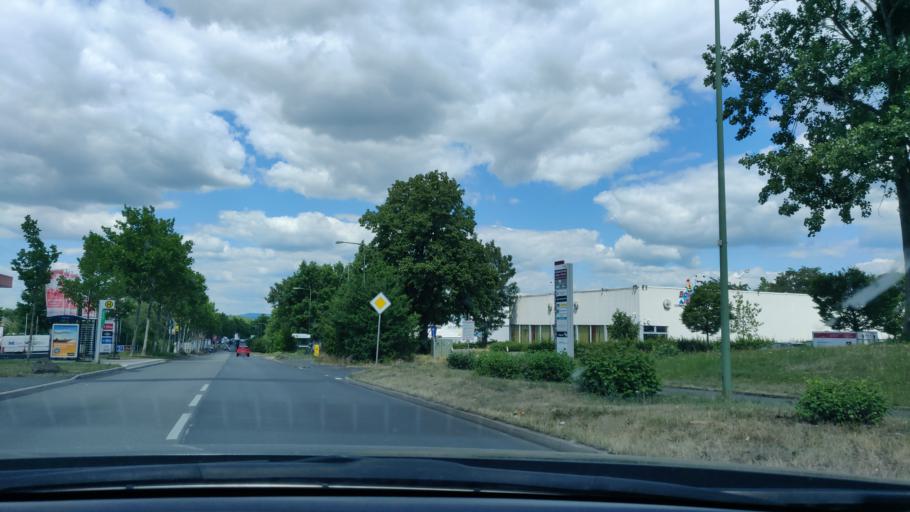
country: DE
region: Hesse
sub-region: Regierungsbezirk Kassel
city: Fuldabruck
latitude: 51.2828
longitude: 9.5017
